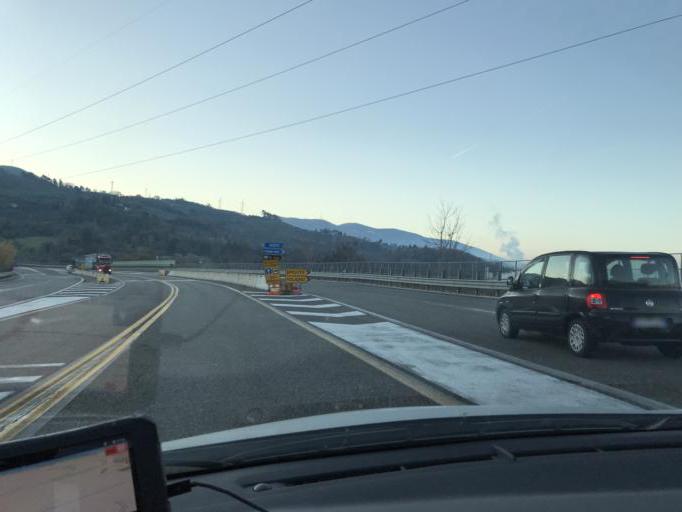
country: IT
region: Umbria
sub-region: Provincia di Terni
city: Terni
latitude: 42.5772
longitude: 12.6806
